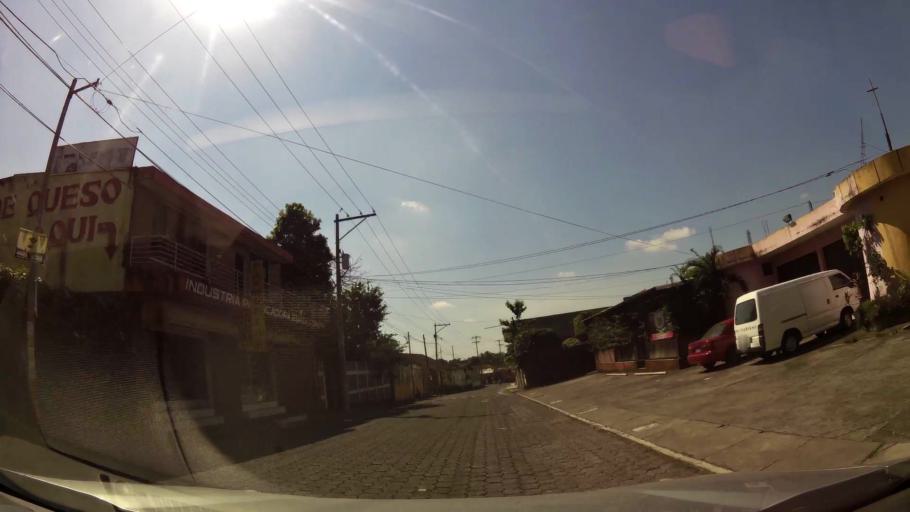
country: GT
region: Suchitepeque
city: Mazatenango
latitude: 14.5356
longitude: -91.4990
